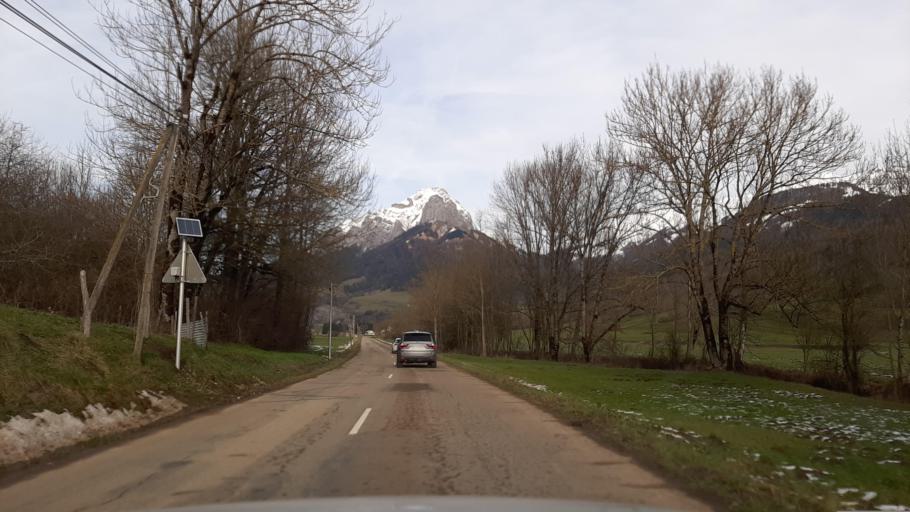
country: FR
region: Rhone-Alpes
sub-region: Departement de la Savoie
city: Gresy-sur-Isere
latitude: 45.6335
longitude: 6.1583
